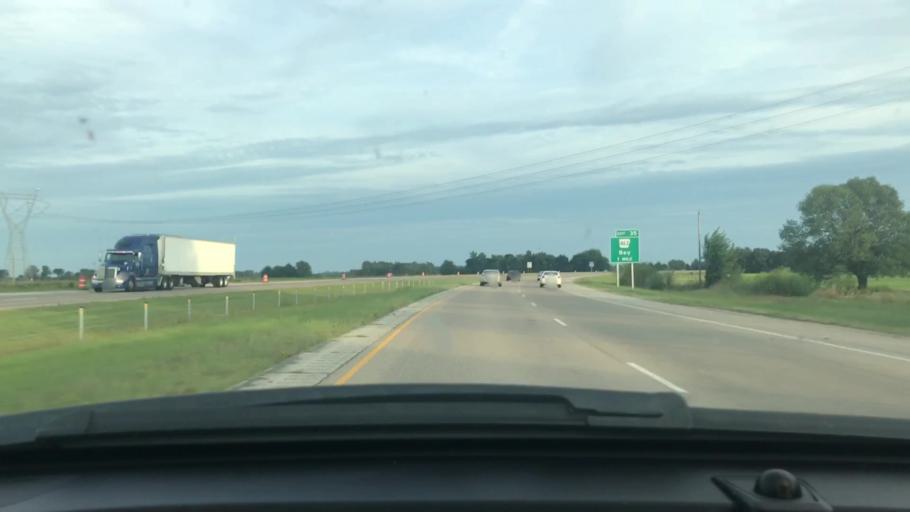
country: US
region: Arkansas
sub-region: Craighead County
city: Bay
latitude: 35.7746
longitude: -90.5792
